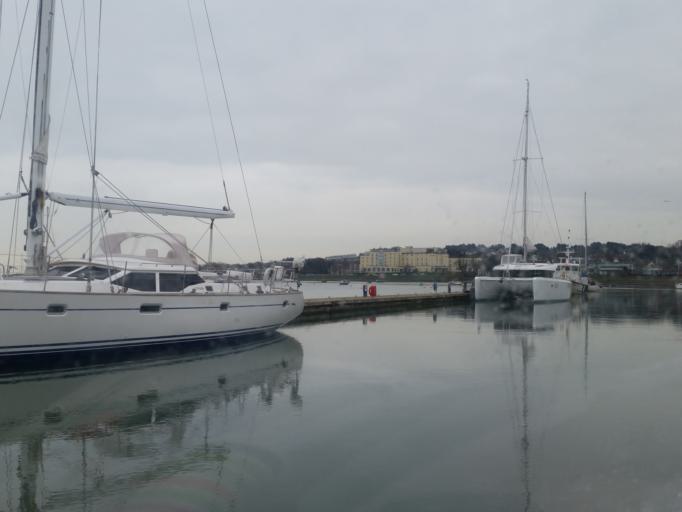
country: IE
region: Leinster
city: Malahide
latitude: 53.4554
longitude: -6.1517
